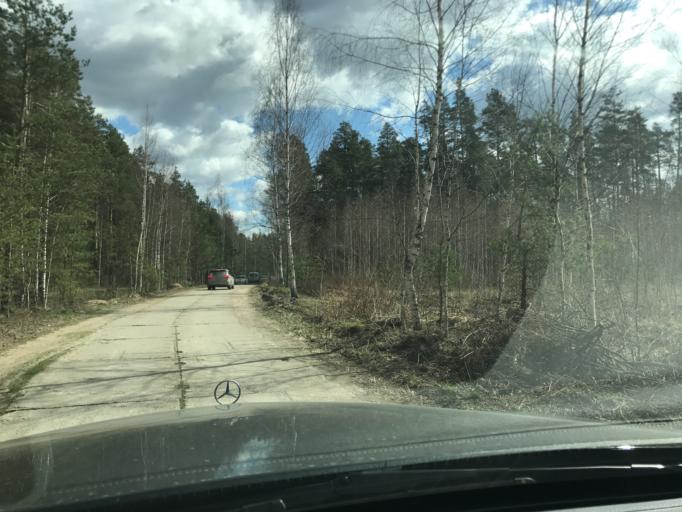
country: RU
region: Moskovskaya
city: Vereya
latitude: 55.8407
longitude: 39.1032
